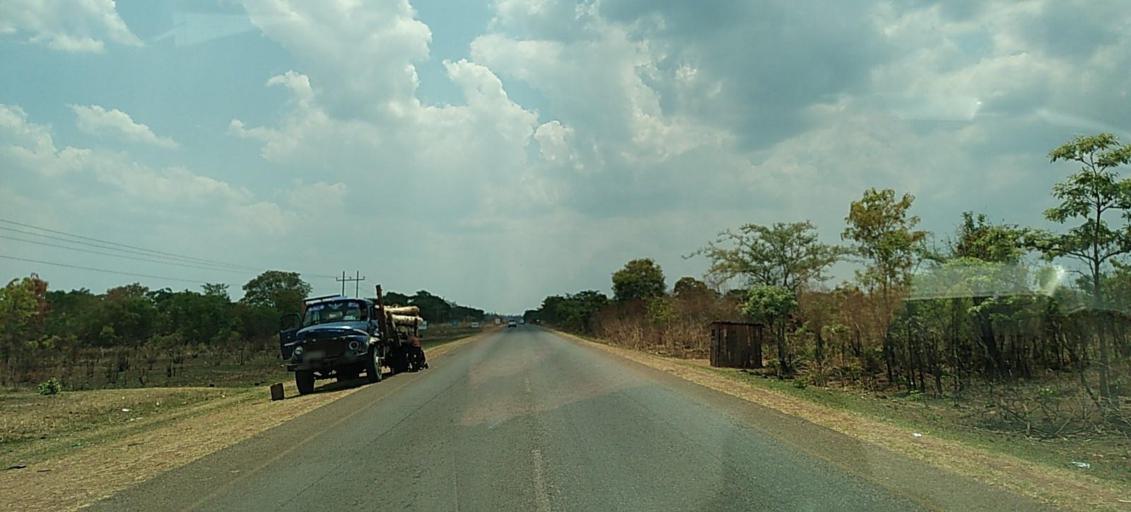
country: ZM
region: Copperbelt
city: Kalulushi
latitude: -12.8360
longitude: 27.9497
